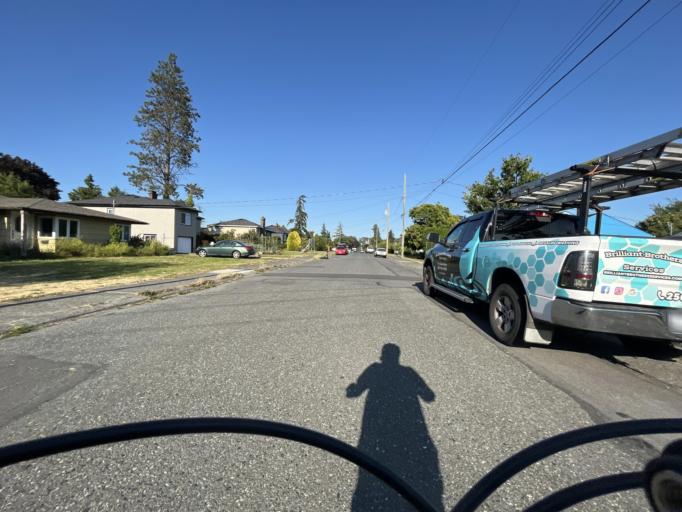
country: CA
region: British Columbia
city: Oak Bay
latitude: 48.4377
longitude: -123.3239
